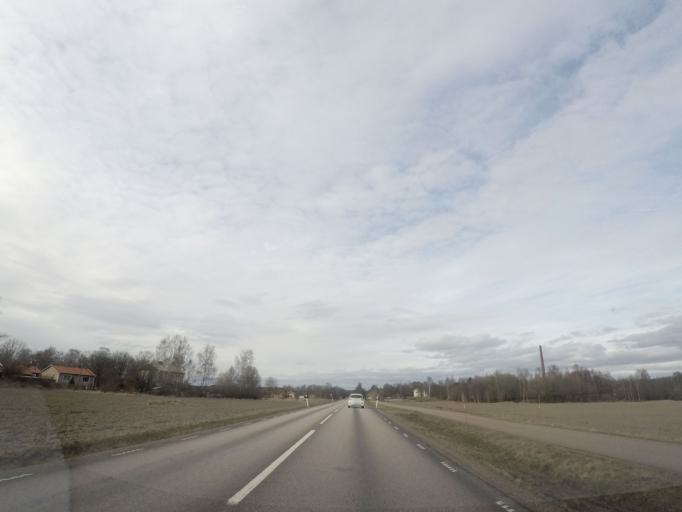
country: SE
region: Vaestmanland
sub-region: Hallstahammars Kommun
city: Hallstahammar
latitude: 59.5803
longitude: 16.2114
